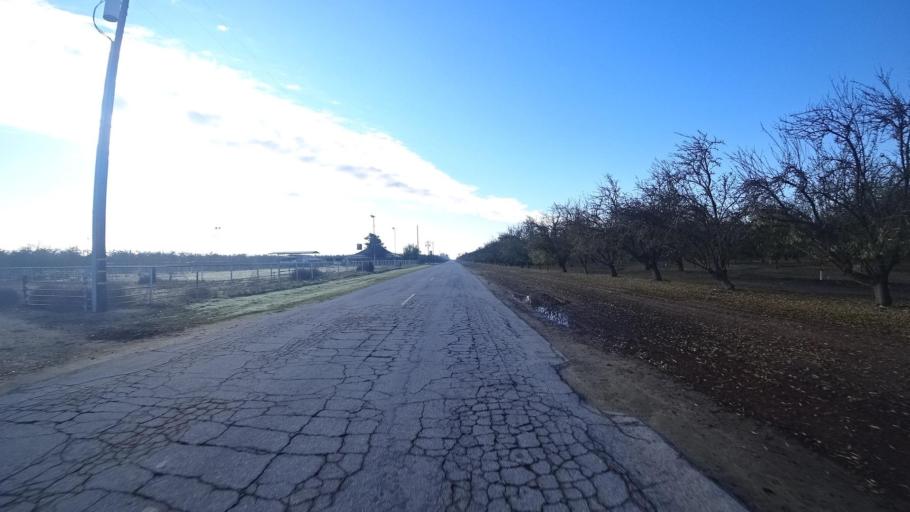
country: US
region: California
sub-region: Kern County
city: Delano
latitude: 35.7286
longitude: -119.3302
